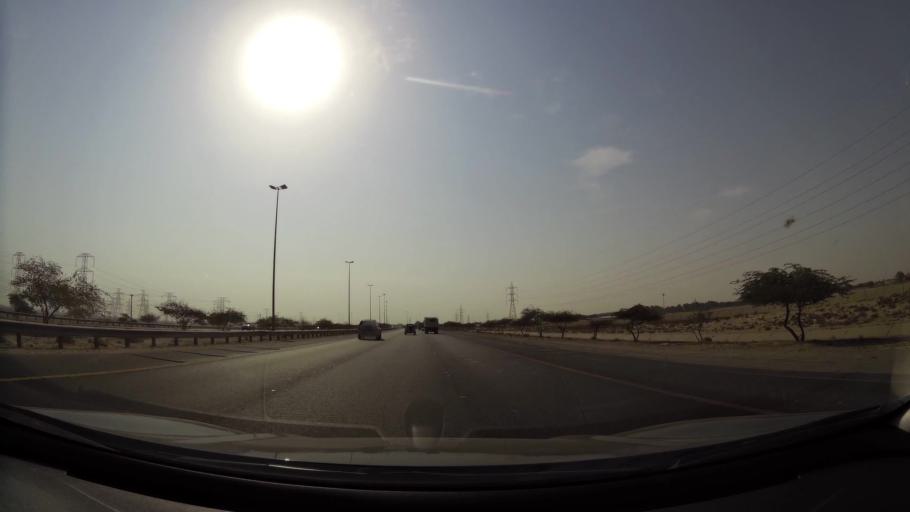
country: KW
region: Al Ahmadi
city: Al Ahmadi
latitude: 28.9678
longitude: 48.1159
